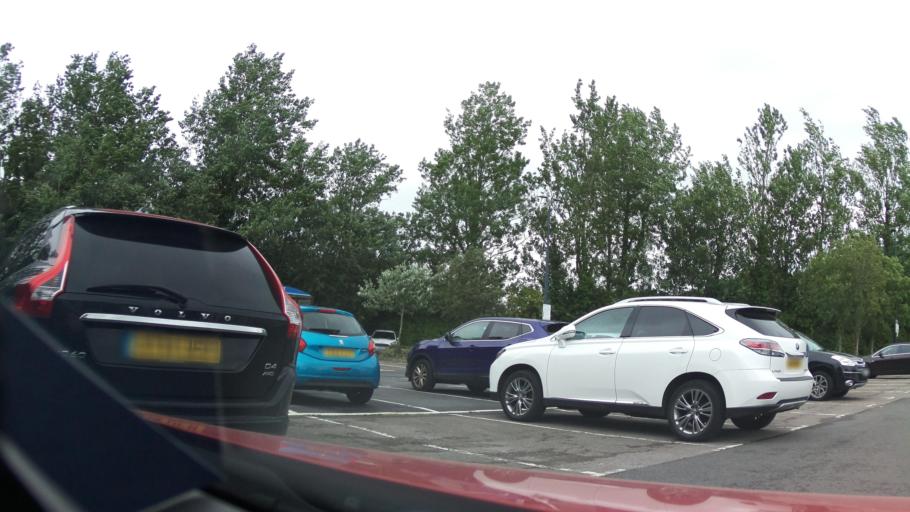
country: GB
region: Wales
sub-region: Vale of Glamorgan
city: Penarth
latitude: 51.4458
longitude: -3.1864
